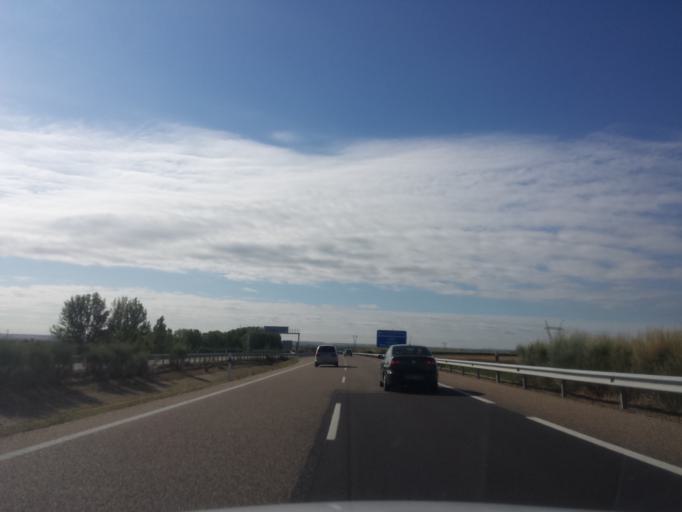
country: ES
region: Castille and Leon
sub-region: Provincia de Leon
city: Villamanan
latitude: 42.3156
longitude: -5.6034
